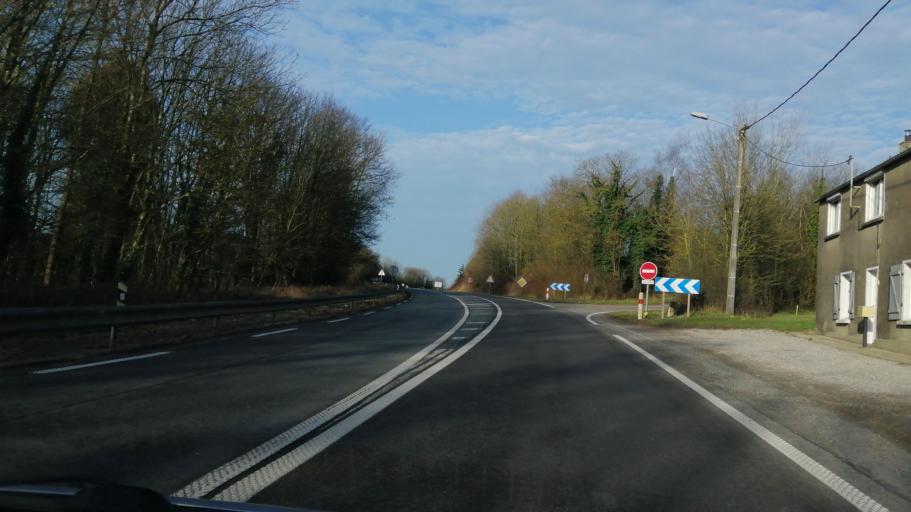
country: FR
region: Nord-Pas-de-Calais
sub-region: Departement du Pas-de-Calais
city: Licques
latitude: 50.7326
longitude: 1.8827
